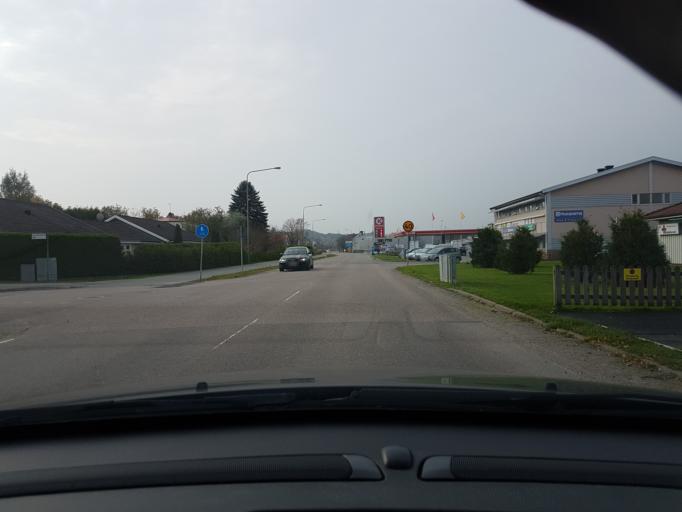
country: SE
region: Vaestra Goetaland
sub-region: Ale Kommun
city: Alvangen
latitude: 57.9605
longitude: 12.1278
